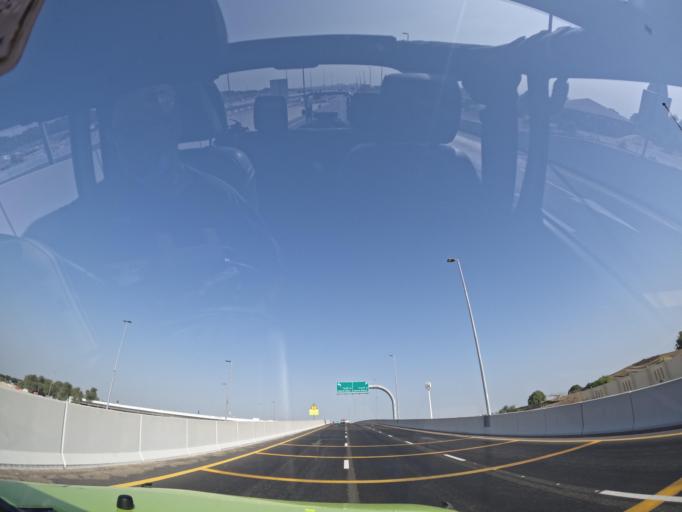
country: AE
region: Dubai
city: Dubai
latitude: 25.1496
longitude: 55.3411
